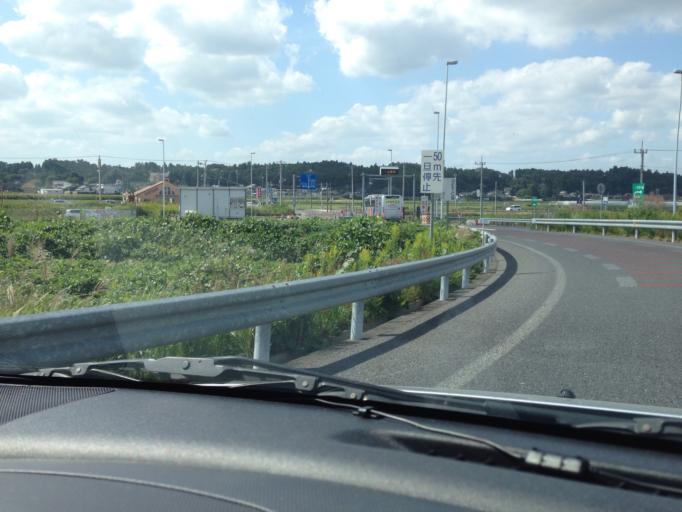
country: JP
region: Ibaraki
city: Mito-shi
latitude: 36.4185
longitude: 140.4260
